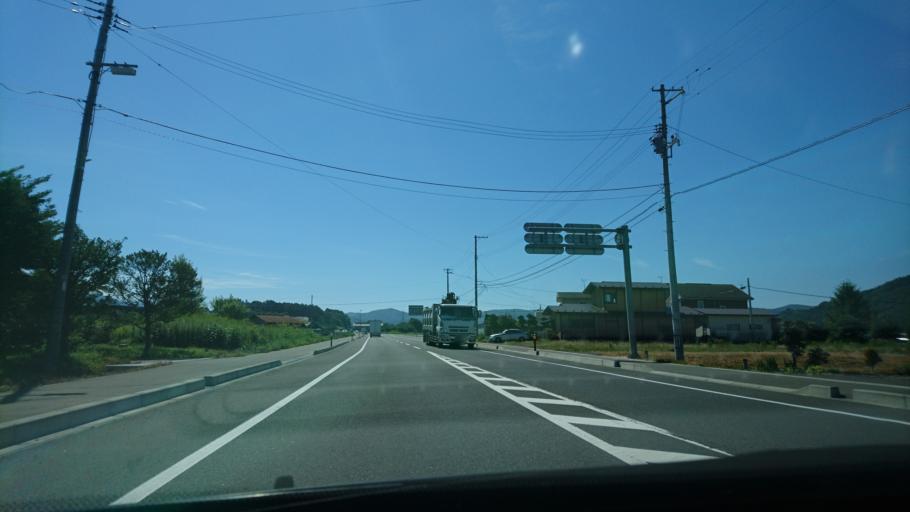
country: JP
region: Iwate
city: Tono
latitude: 39.3105
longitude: 141.5709
